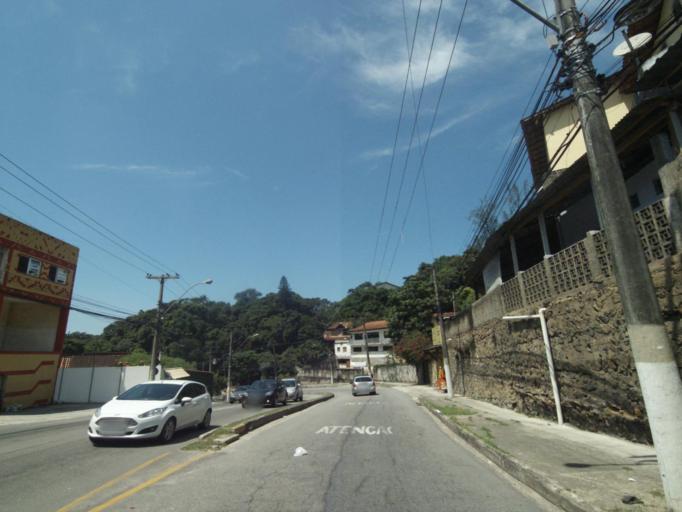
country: BR
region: Rio de Janeiro
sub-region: Niteroi
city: Niteroi
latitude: -22.9042
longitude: -43.0502
